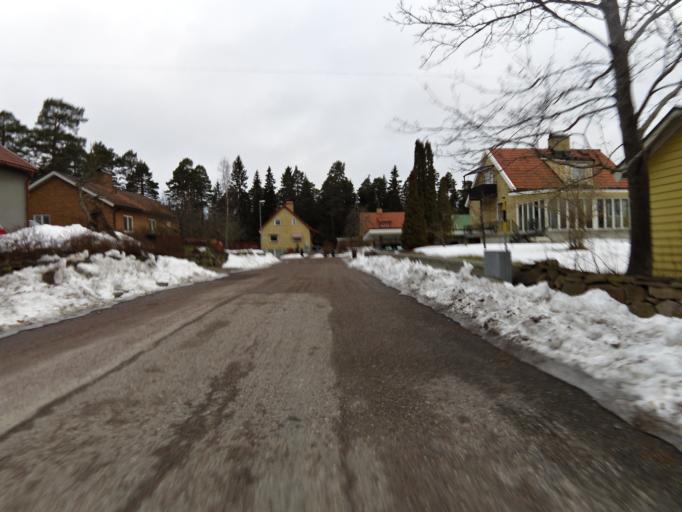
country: SE
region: Gaevleborg
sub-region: Gavle Kommun
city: Gavle
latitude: 60.6613
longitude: 17.1295
